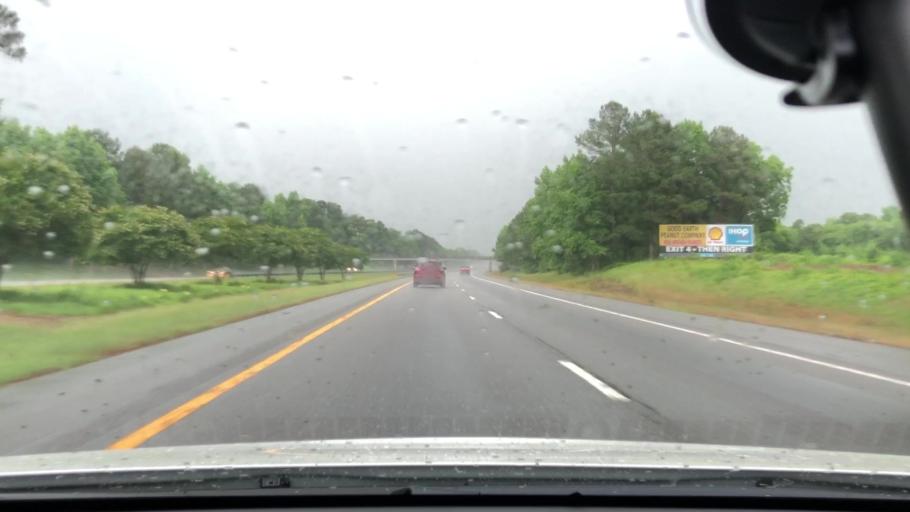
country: US
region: North Carolina
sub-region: Halifax County
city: Halifax
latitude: 36.3308
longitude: -77.6999
